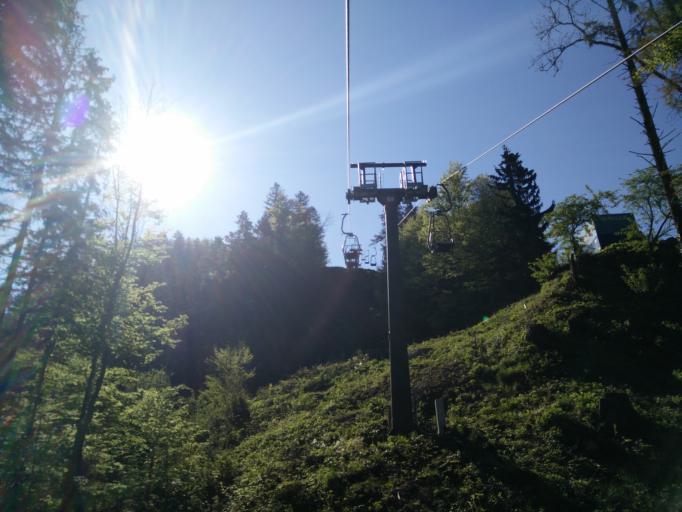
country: AT
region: Tyrol
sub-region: Politischer Bezirk Kufstein
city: Kufstein
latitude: 47.5873
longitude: 12.1912
